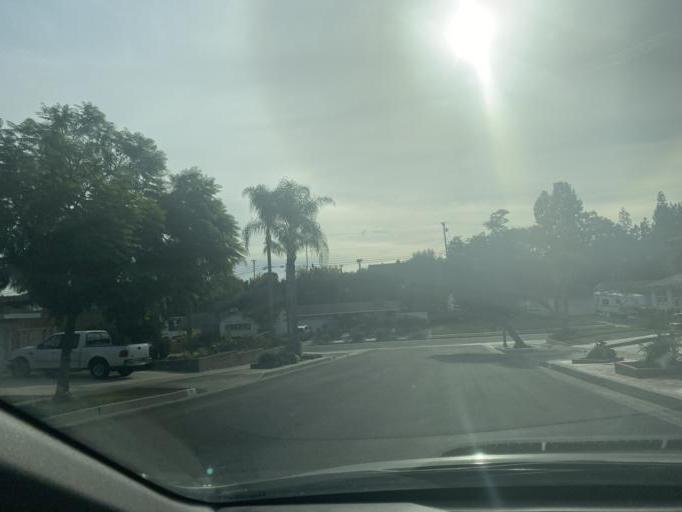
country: US
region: California
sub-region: Orange County
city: Brea
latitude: 33.9052
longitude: -117.8989
